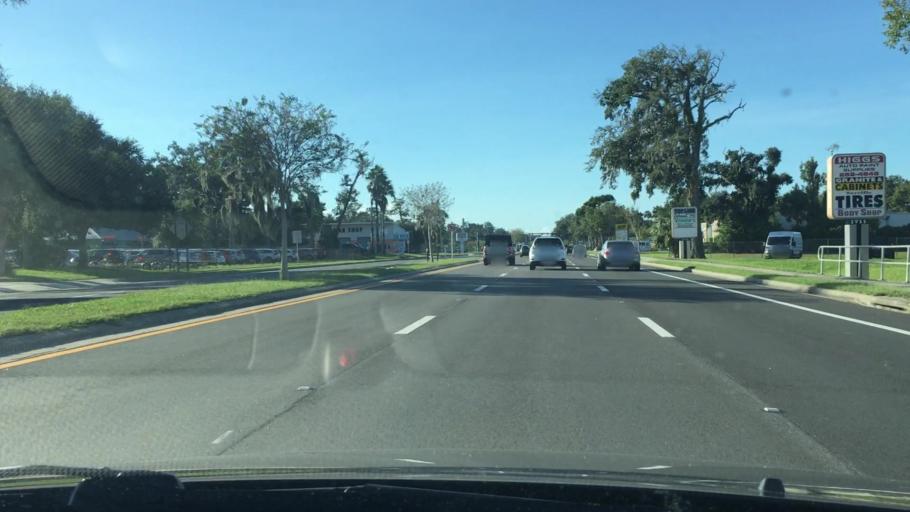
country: US
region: Florida
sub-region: Volusia County
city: Holly Hill
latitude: 29.2426
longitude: -81.0613
